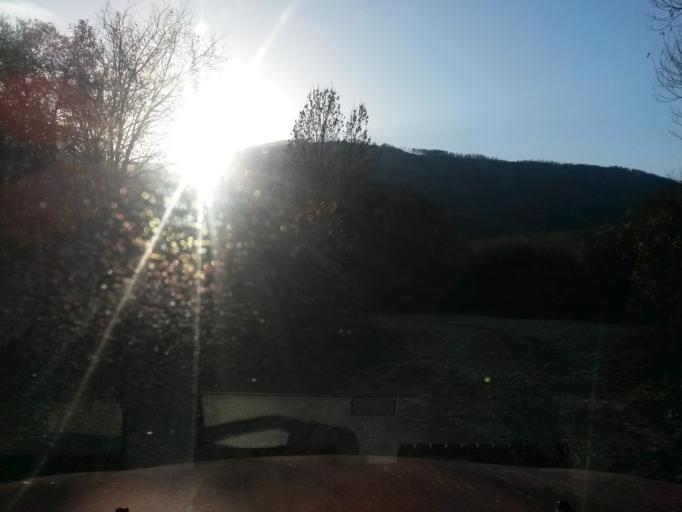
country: SK
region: Kosicky
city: Roznava
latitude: 48.6966
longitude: 20.5127
